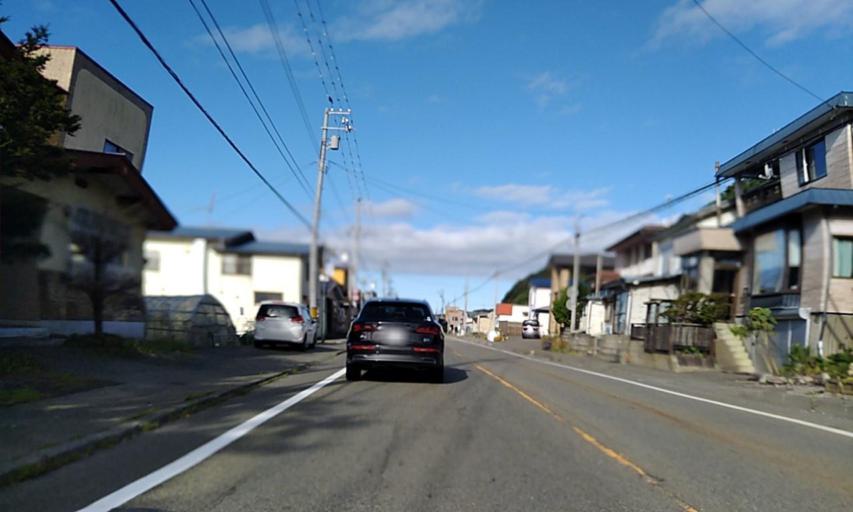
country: JP
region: Hokkaido
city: Shizunai-furukawacho
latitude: 42.2507
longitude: 142.5514
